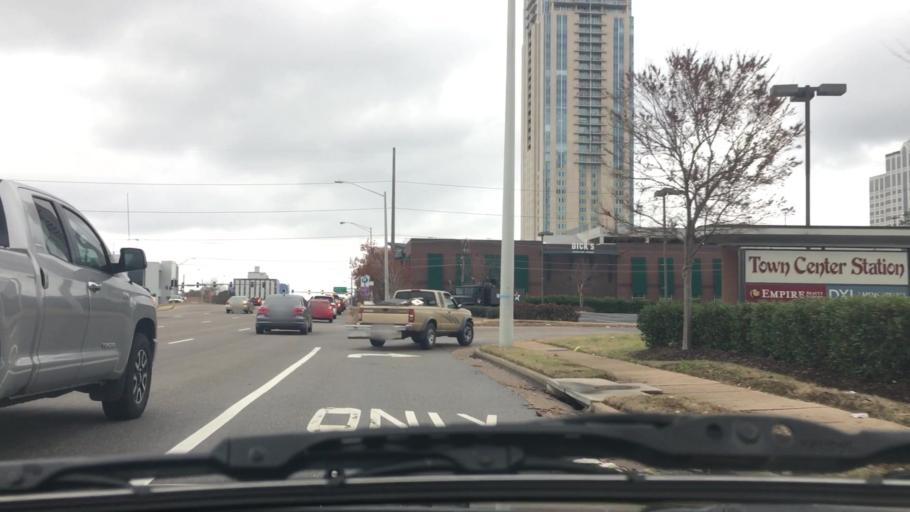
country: US
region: Virginia
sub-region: City of Chesapeake
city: Chesapeake
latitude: 36.8387
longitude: -76.1367
